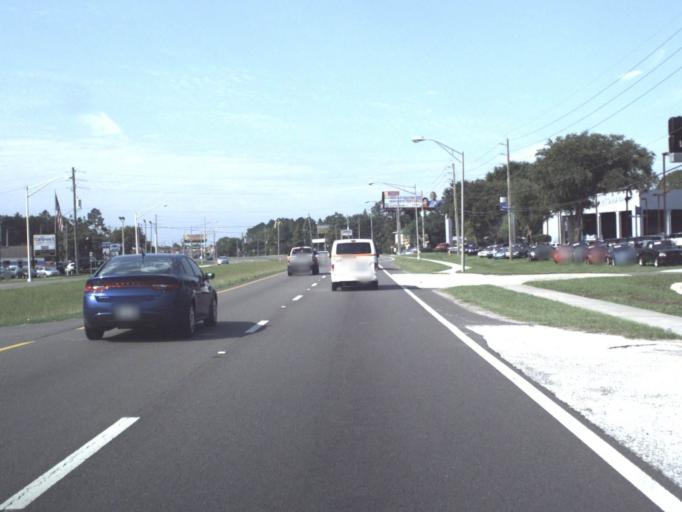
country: US
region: Florida
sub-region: Clay County
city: Bellair-Meadowbrook Terrace
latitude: 30.2093
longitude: -81.7386
